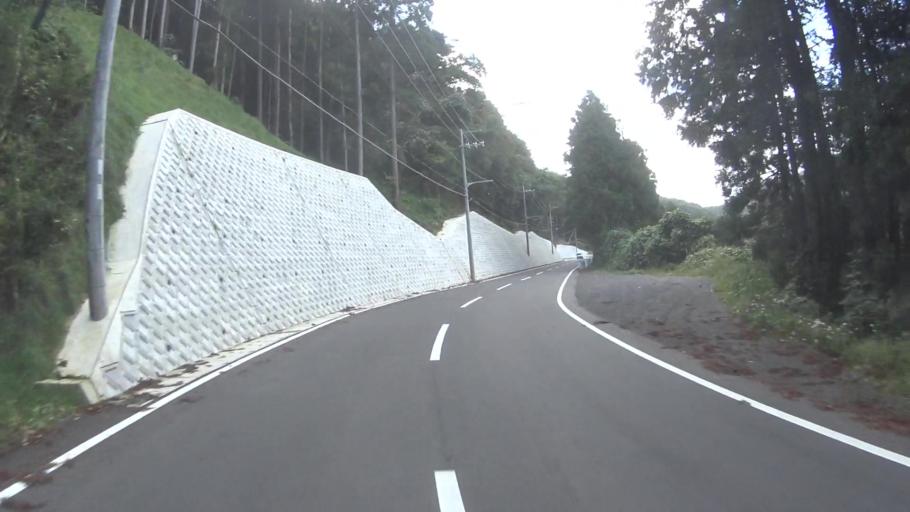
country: JP
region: Kyoto
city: Maizuru
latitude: 35.5568
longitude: 135.4374
